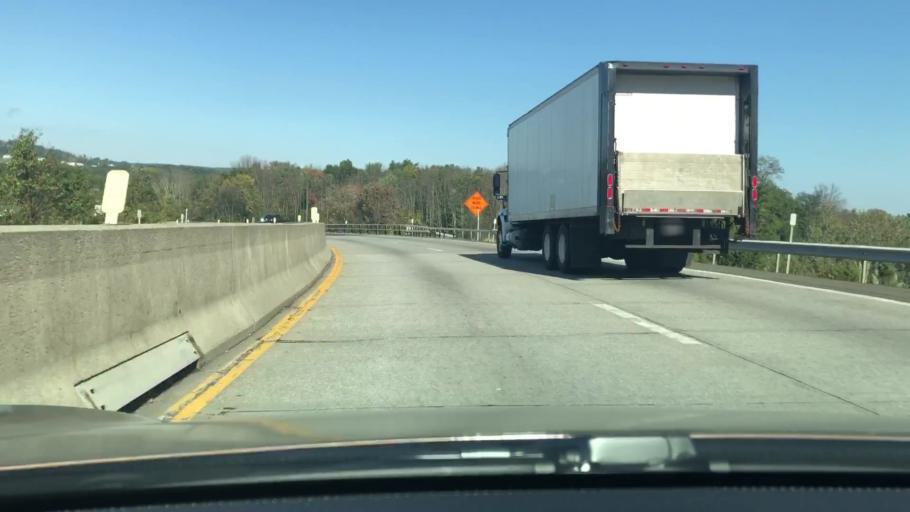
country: US
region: New York
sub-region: Orange County
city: Central Valley
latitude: 41.3101
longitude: -74.1217
